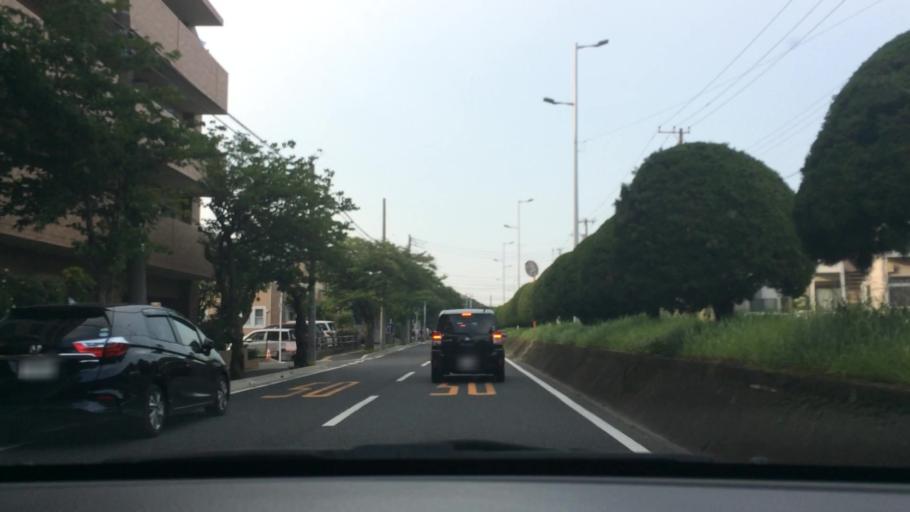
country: JP
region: Tokyo
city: Urayasu
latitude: 35.6491
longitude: 139.8932
